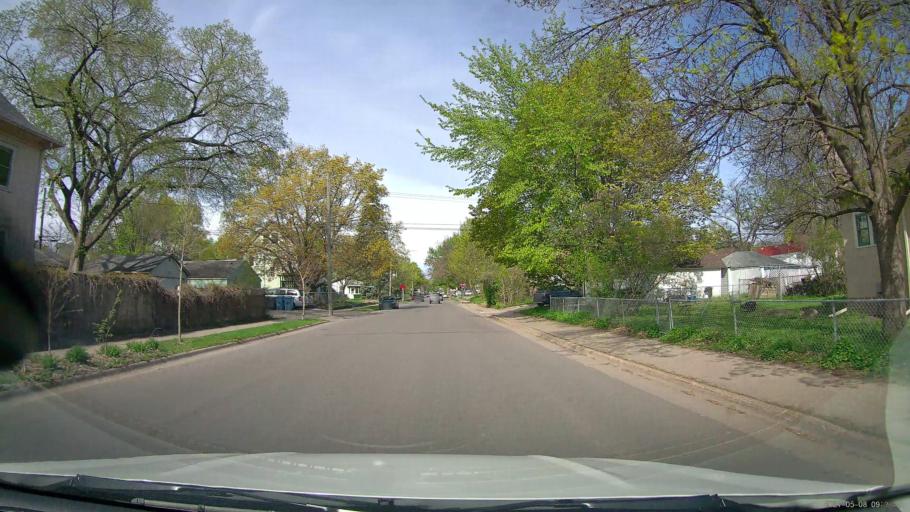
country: US
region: Minnesota
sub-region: Hennepin County
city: Minneapolis
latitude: 44.9396
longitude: -93.2232
